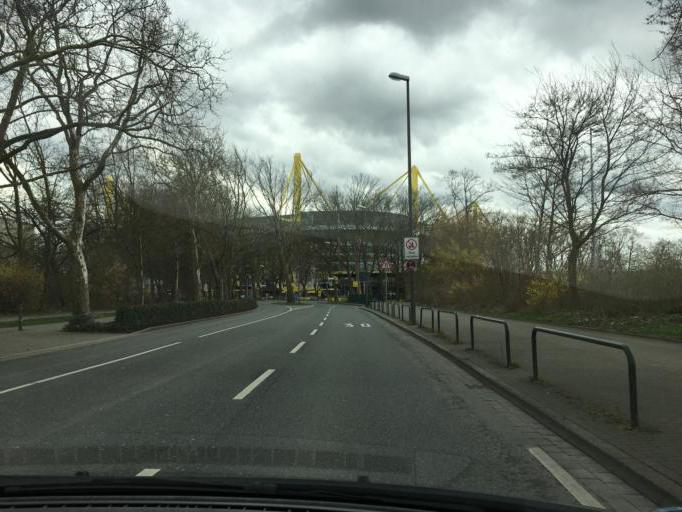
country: DE
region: North Rhine-Westphalia
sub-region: Regierungsbezirk Arnsberg
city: Dortmund
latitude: 51.4955
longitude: 7.4485
